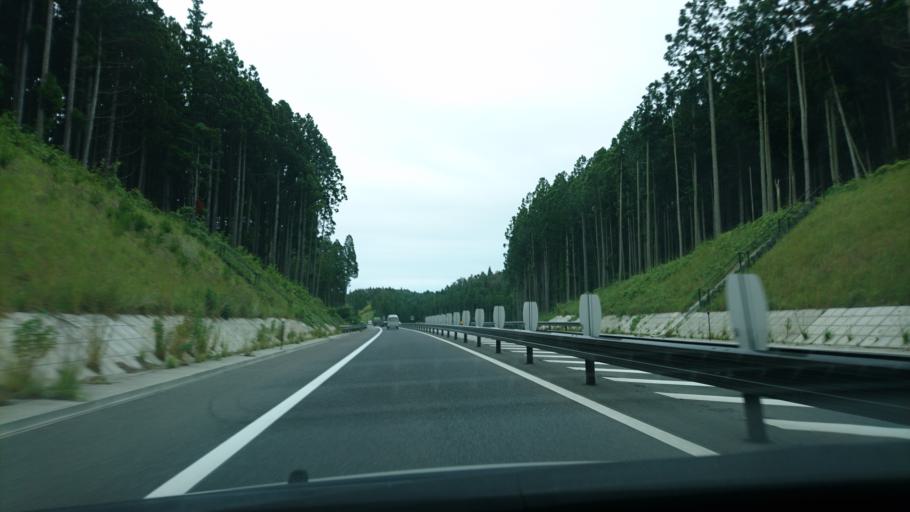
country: JP
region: Miyagi
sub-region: Oshika Gun
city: Onagawa Cho
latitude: 38.6927
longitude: 141.4093
